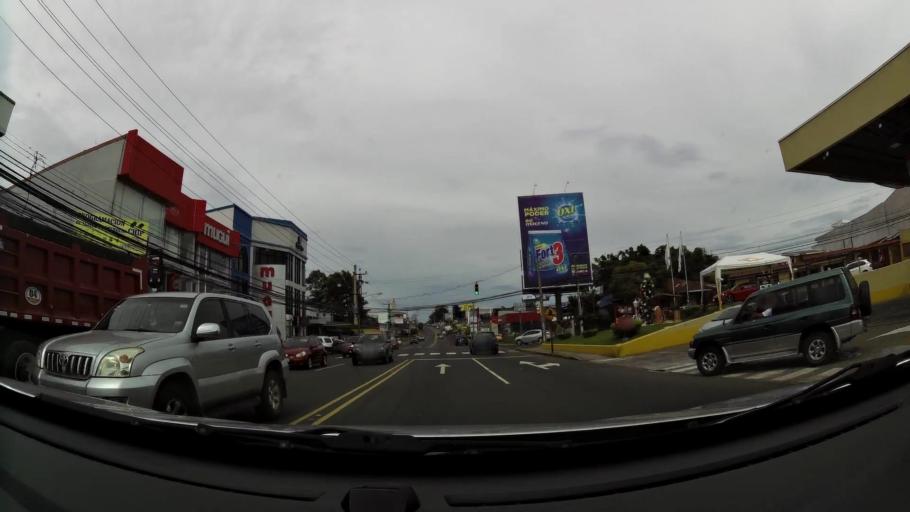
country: CR
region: San Jose
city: Curridabat
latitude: 9.9208
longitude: -84.0362
